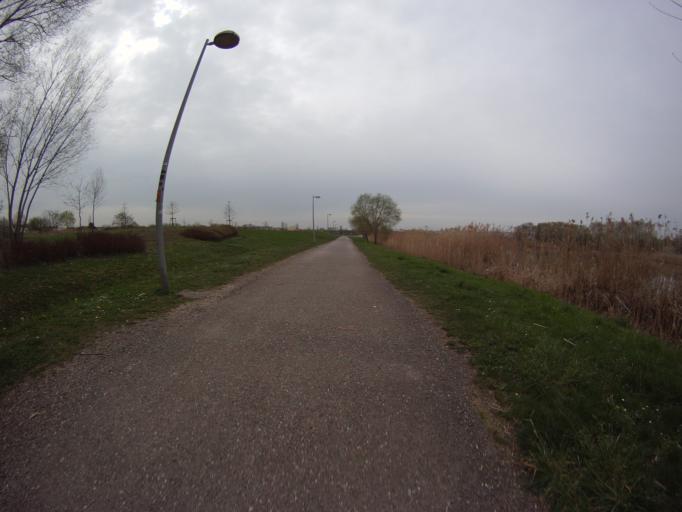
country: FR
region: Lorraine
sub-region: Departement de Meurthe-et-Moselle
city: Saint-Max
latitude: 48.6950
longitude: 6.2075
